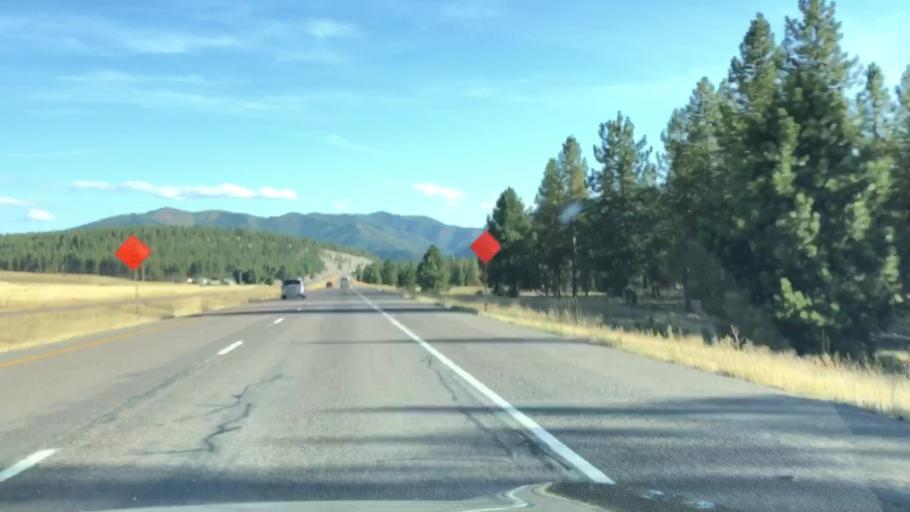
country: US
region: Montana
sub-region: Mineral County
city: Superior
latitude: 47.0348
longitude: -114.7458
